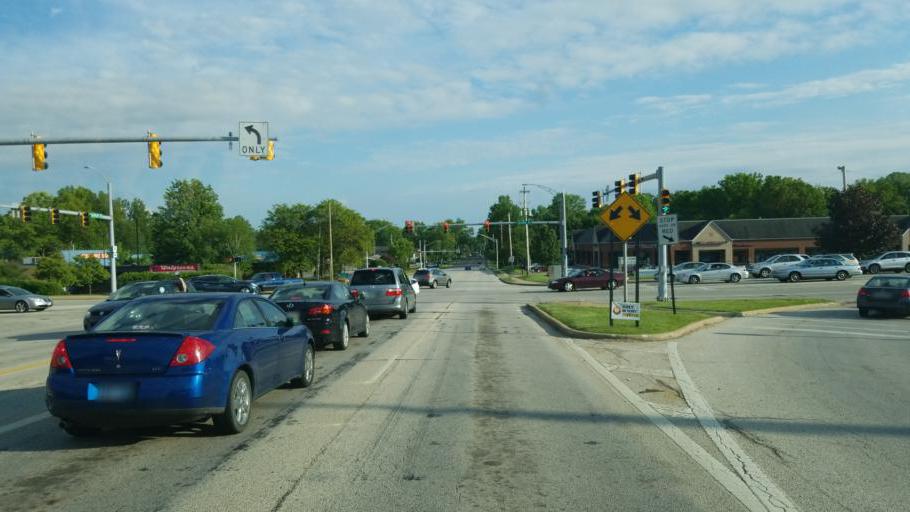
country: US
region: Ohio
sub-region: Summit County
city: Stow
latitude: 41.1672
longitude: -81.4405
